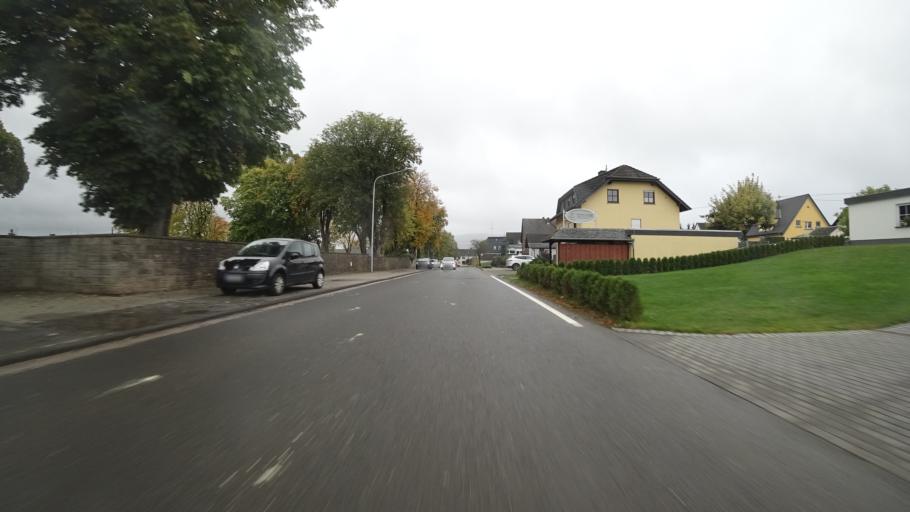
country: DE
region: Rheinland-Pfalz
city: Rheinbollen
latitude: 50.0112
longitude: 7.6692
